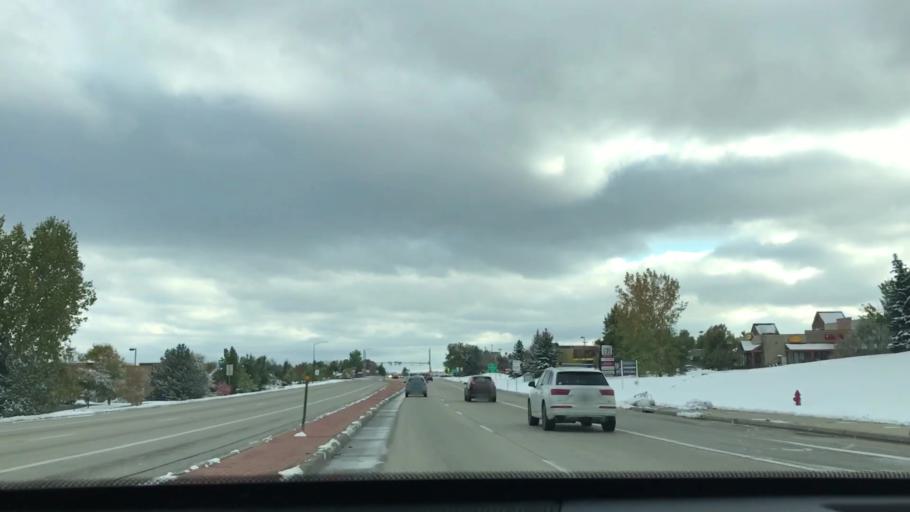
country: US
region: Colorado
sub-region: Boulder County
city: Lafayette
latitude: 40.0036
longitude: -105.1029
